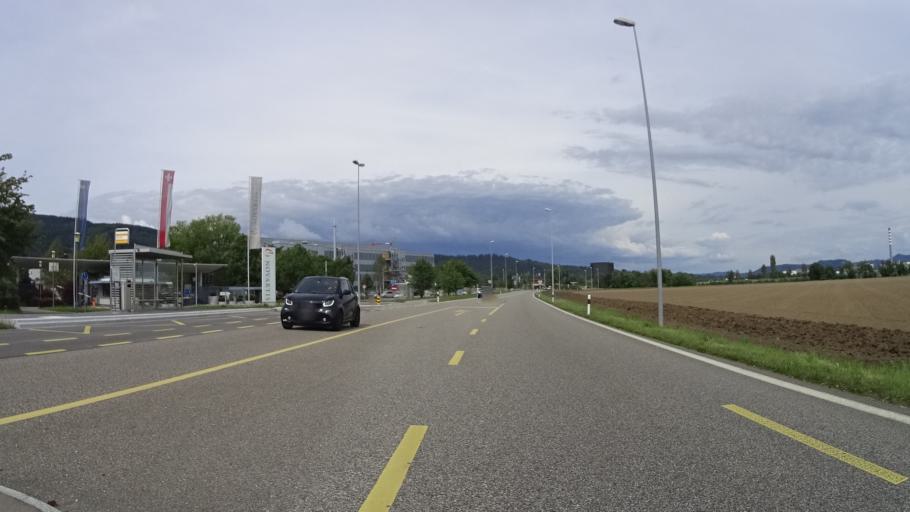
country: CH
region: Aargau
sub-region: Bezirk Rheinfelden
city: Stein
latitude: 47.5506
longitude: 7.9572
